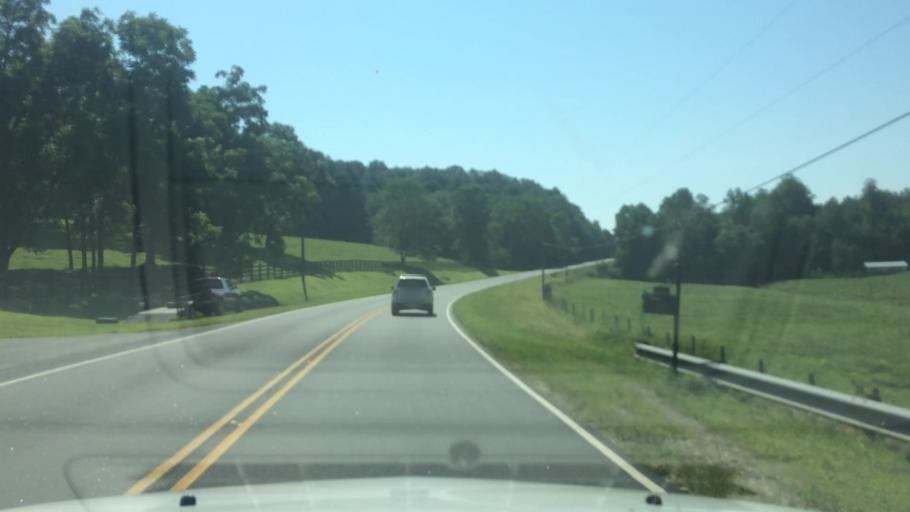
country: US
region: North Carolina
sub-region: Caldwell County
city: Hudson
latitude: 35.9152
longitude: -81.4499
